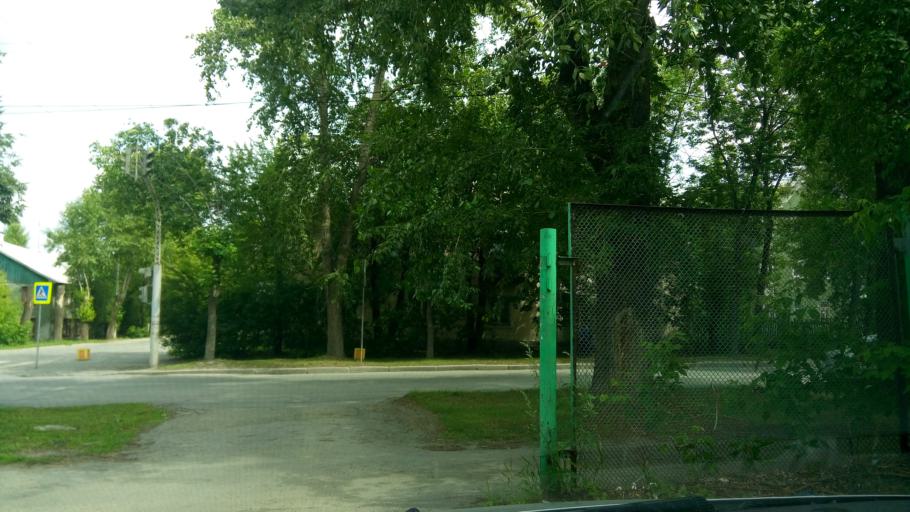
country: RU
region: Sverdlovsk
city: Yekaterinburg
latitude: 56.8857
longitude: 60.6251
